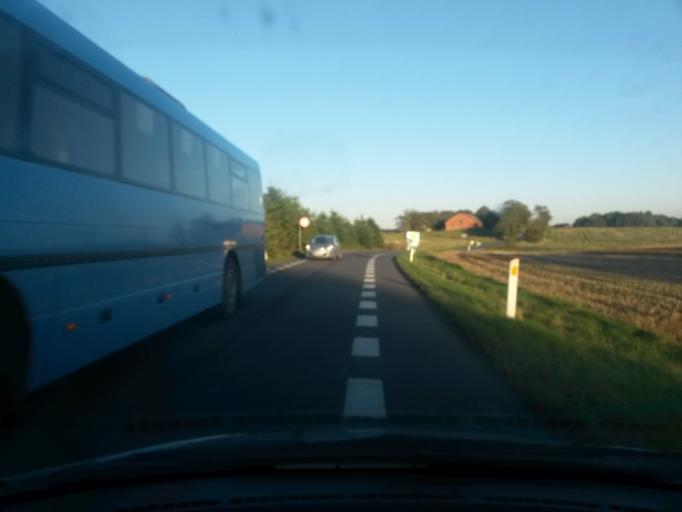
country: DK
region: Central Jutland
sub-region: Silkeborg Kommune
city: Kjellerup
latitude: 56.2892
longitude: 9.3708
